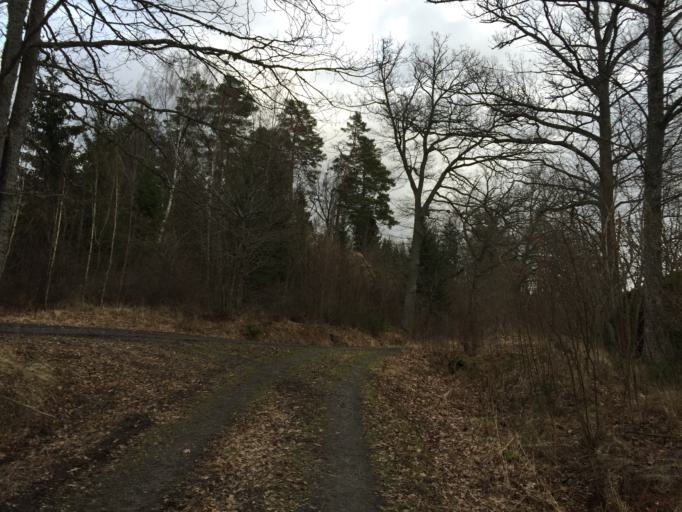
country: SE
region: Stockholm
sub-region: Salems Kommun
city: Ronninge
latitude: 59.2496
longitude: 17.7068
